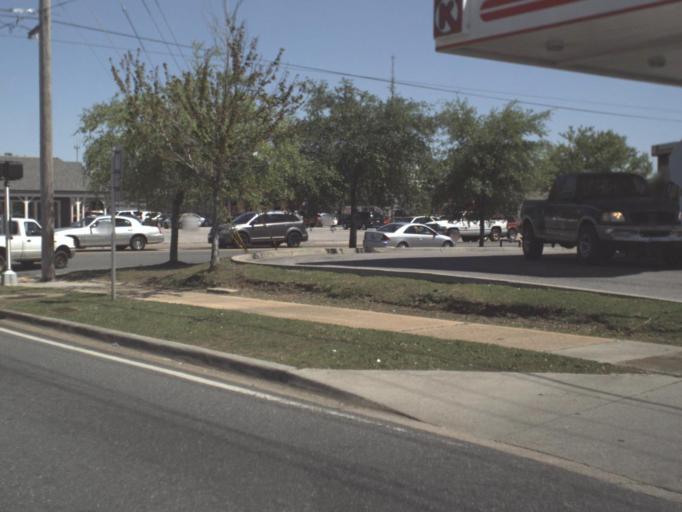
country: US
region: Florida
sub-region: Escambia County
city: Goulding
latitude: 30.4452
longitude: -87.2403
